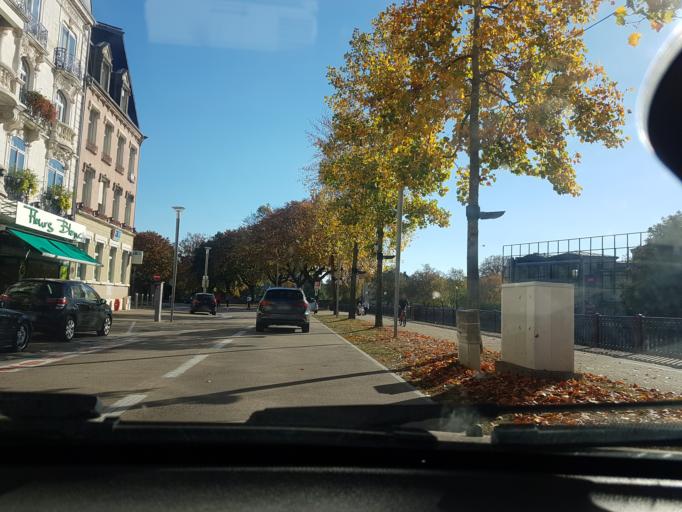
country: FR
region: Franche-Comte
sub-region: Territoire de Belfort
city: Belfort
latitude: 47.6374
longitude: 6.8588
